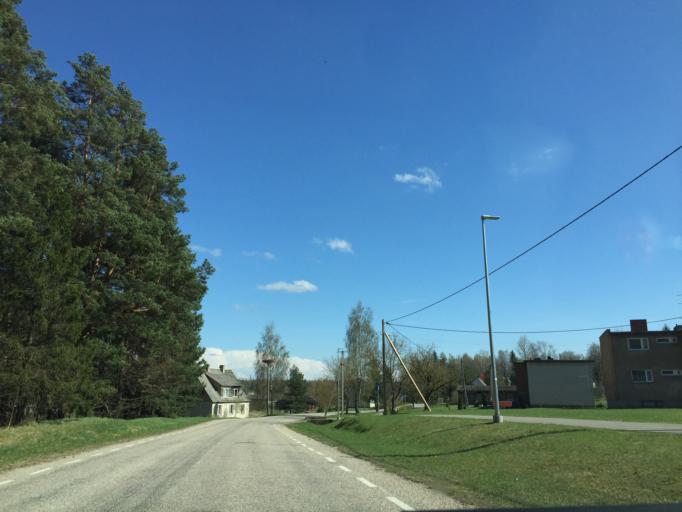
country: EE
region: Valgamaa
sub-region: Valga linn
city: Valga
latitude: 57.8566
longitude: 26.1138
